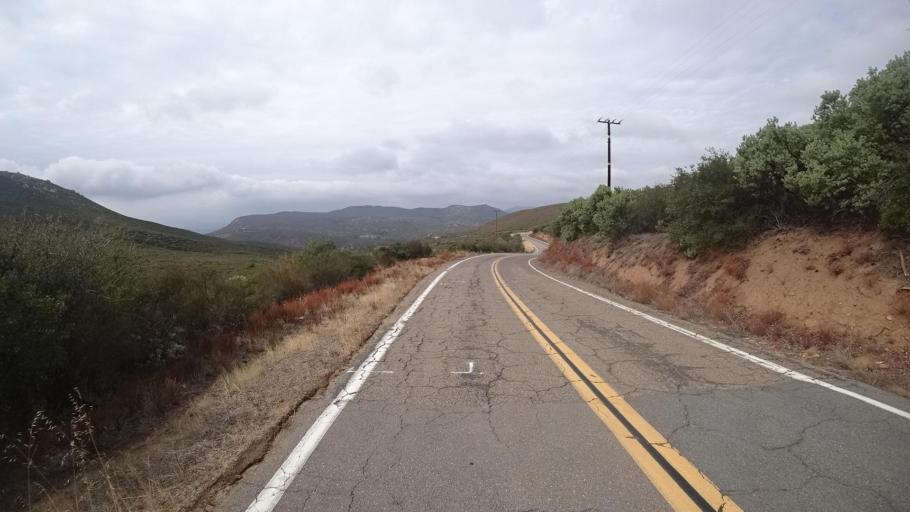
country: US
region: California
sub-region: San Diego County
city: Descanso
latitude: 32.8847
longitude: -116.6479
